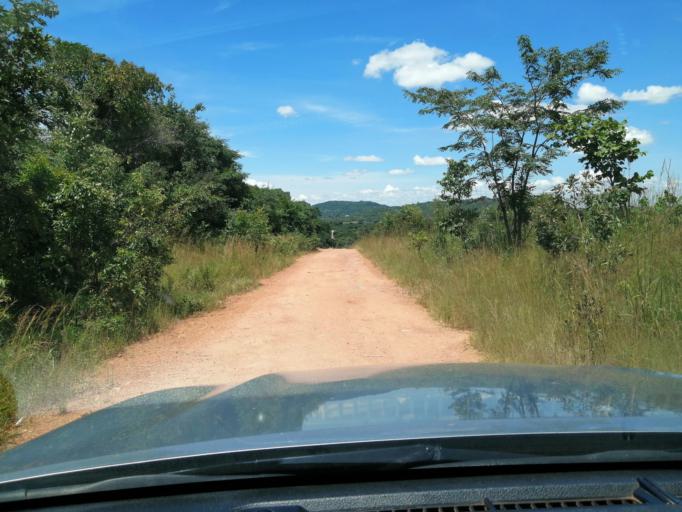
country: ZM
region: Lusaka
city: Lusaka
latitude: -15.1307
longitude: 27.8945
